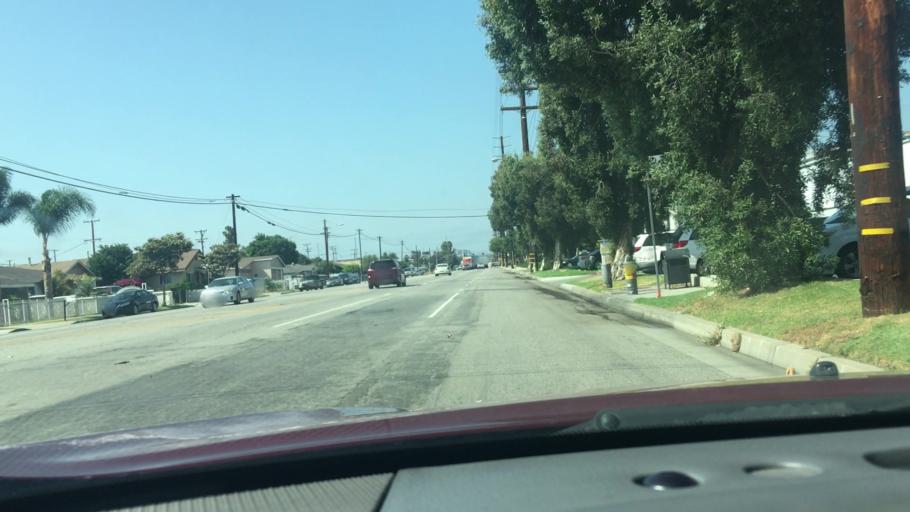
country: US
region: California
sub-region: Los Angeles County
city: Norwalk
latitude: 33.8988
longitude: -118.0465
